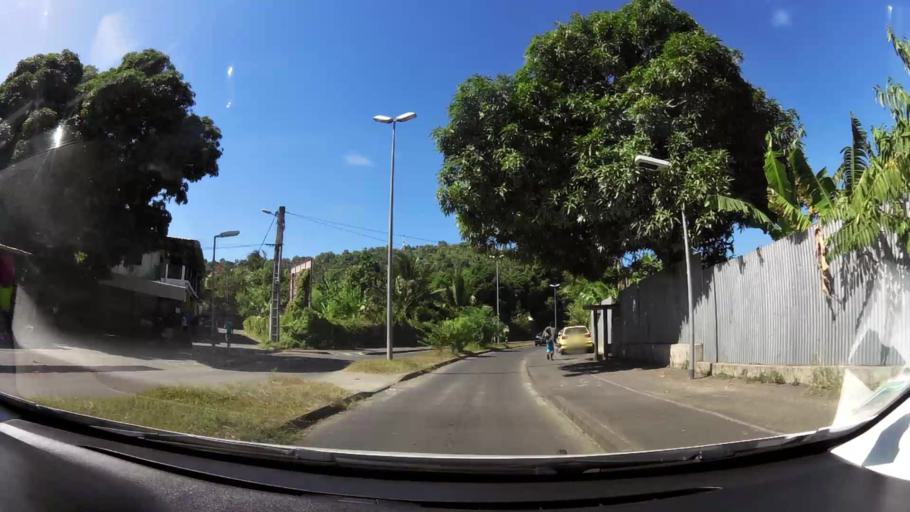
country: YT
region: Pamandzi
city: Pamandzi
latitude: -12.7919
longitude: 45.2811
